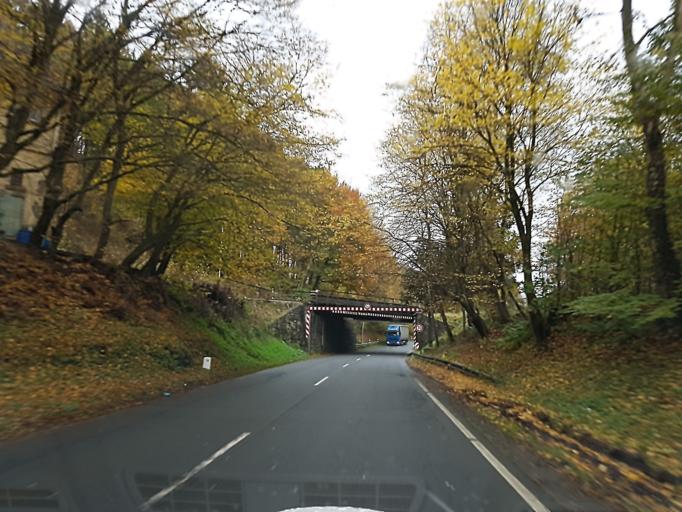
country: DE
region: North Rhine-Westphalia
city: Kierspe
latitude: 51.1887
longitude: 7.5711
